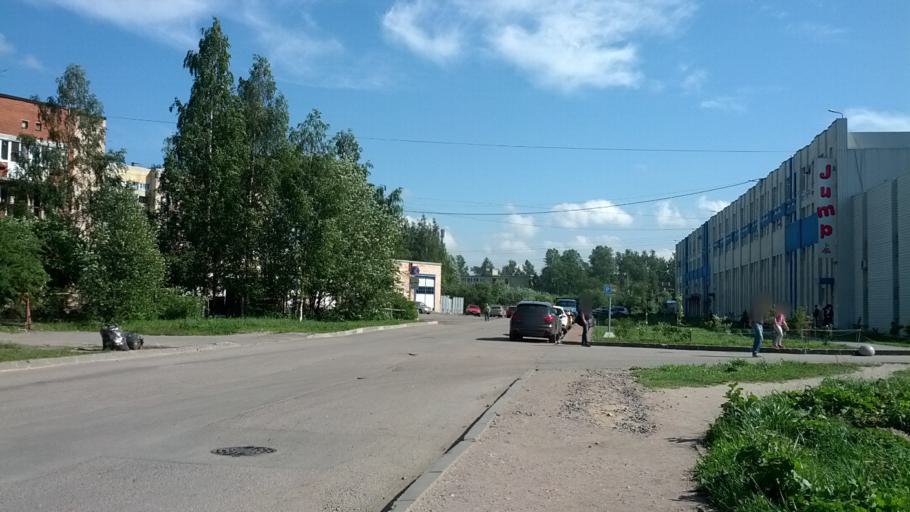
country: RU
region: Leningrad
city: Rybatskoye
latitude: 59.8903
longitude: 30.4818
